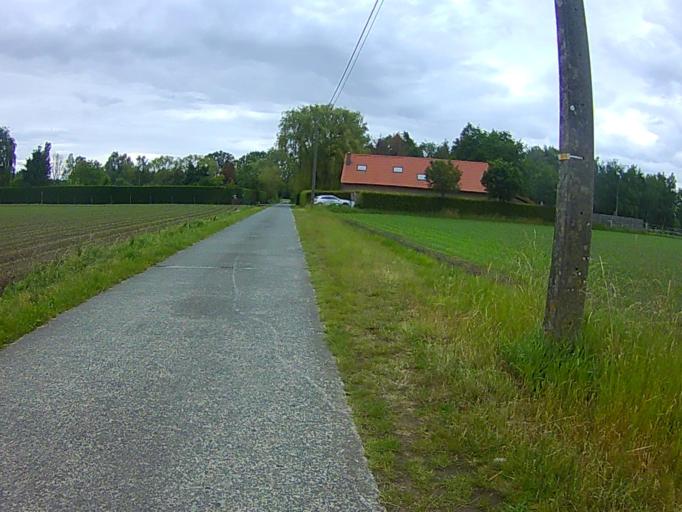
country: BE
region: Flanders
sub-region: Provincie Antwerpen
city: Putte
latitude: 51.0514
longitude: 4.6470
